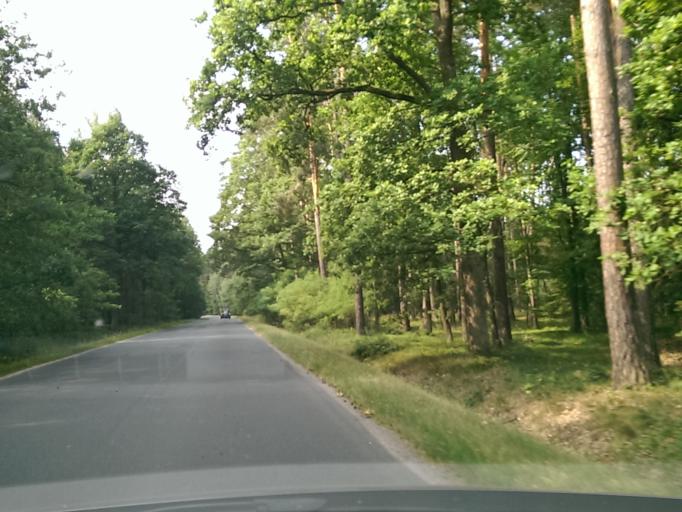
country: CZ
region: Central Bohemia
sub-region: Okres Mlada Boleslav
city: Zd'ar
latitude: 50.5118
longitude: 15.1143
